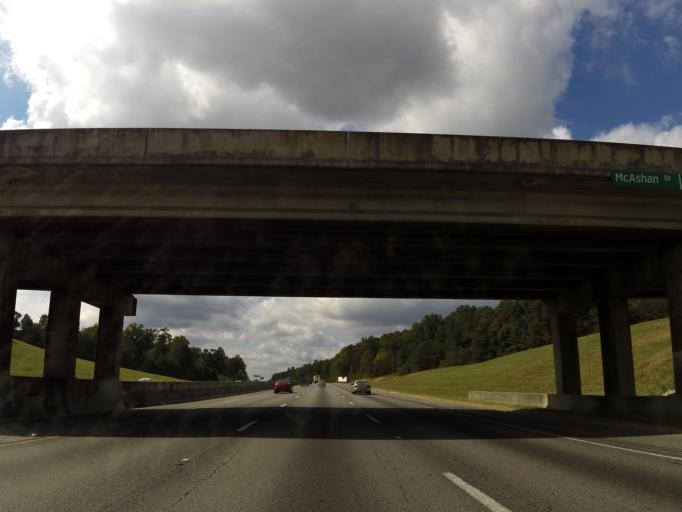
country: US
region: Alabama
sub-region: Tuscaloosa County
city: Lake View
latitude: 33.3245
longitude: -87.0479
